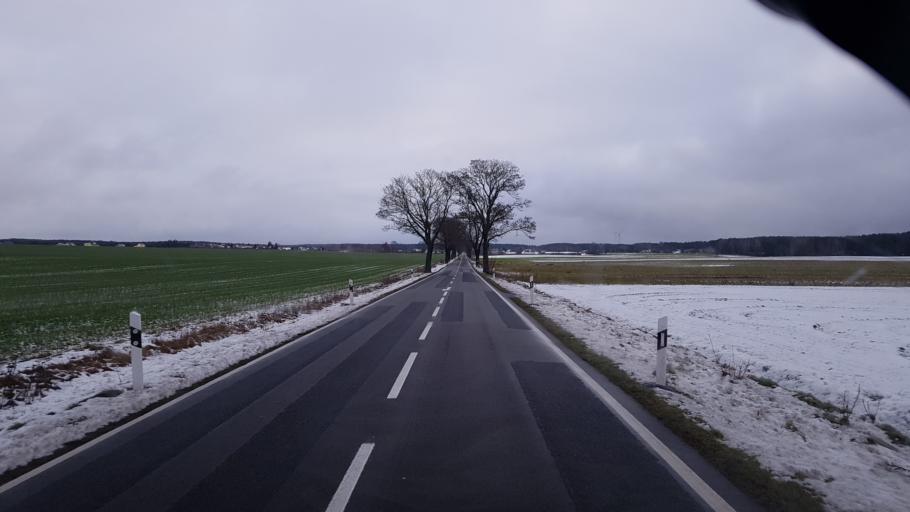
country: DE
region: Brandenburg
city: Tauer
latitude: 51.9786
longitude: 14.5157
